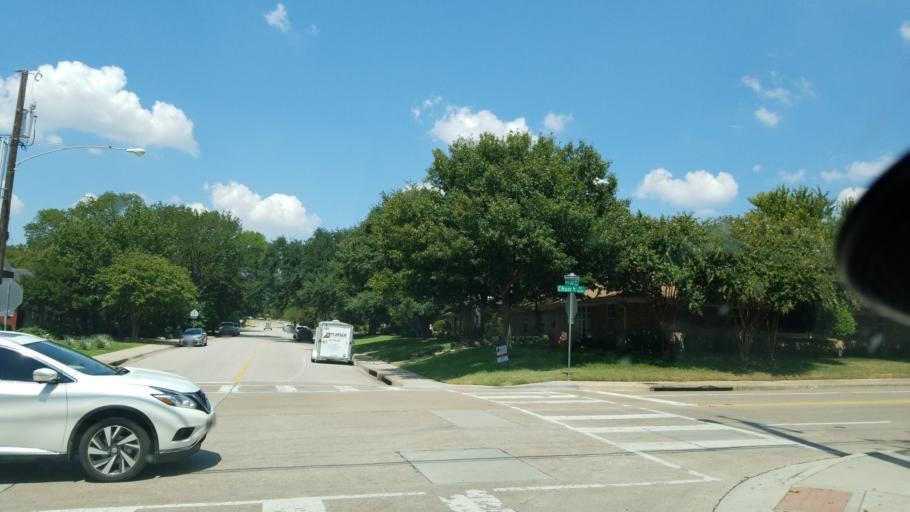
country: US
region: Texas
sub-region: Dallas County
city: Richardson
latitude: 32.8860
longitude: -96.7091
